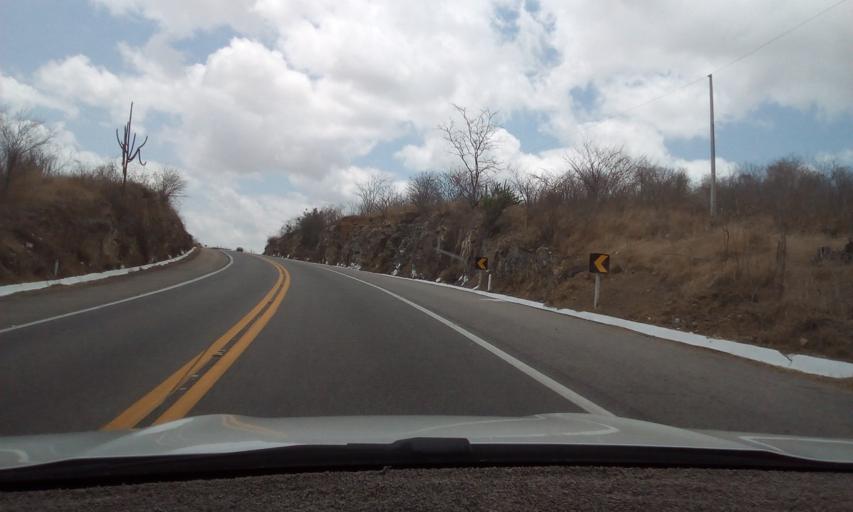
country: BR
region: Pernambuco
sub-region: Taquaritinga Do Norte
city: Taquaritinga do Norte
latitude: -7.6883
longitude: -36.0618
